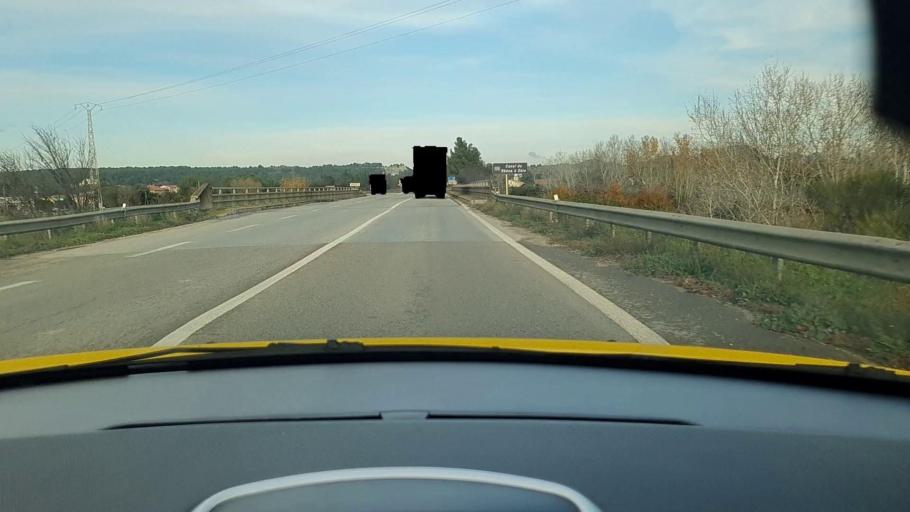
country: FR
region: Languedoc-Roussillon
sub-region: Departement du Gard
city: Beaucaire
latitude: 43.7962
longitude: 4.6100
